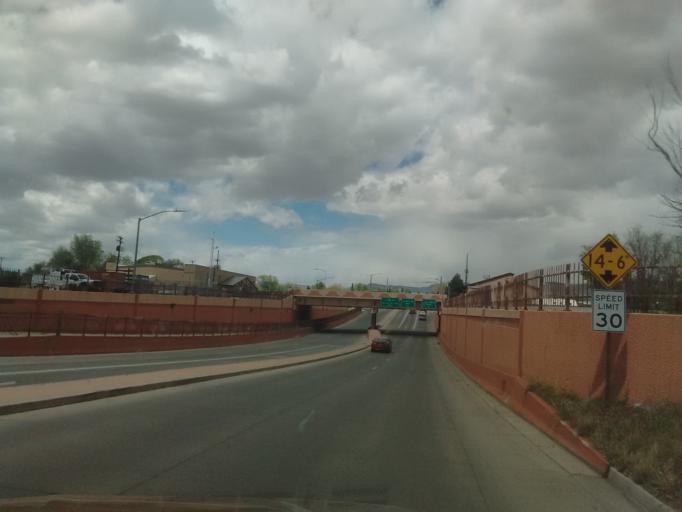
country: US
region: Colorado
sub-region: Mesa County
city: Fruitvale
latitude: 39.0758
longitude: -108.4964
